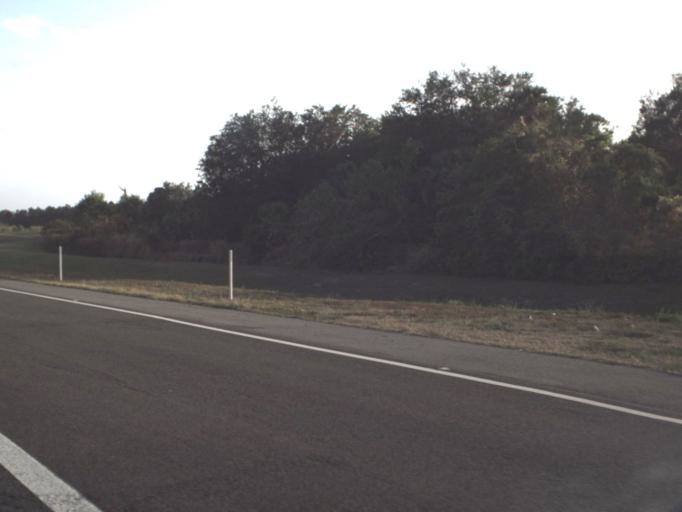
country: US
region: Florida
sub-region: Brevard County
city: Port Saint John
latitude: 28.4589
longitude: -80.8215
